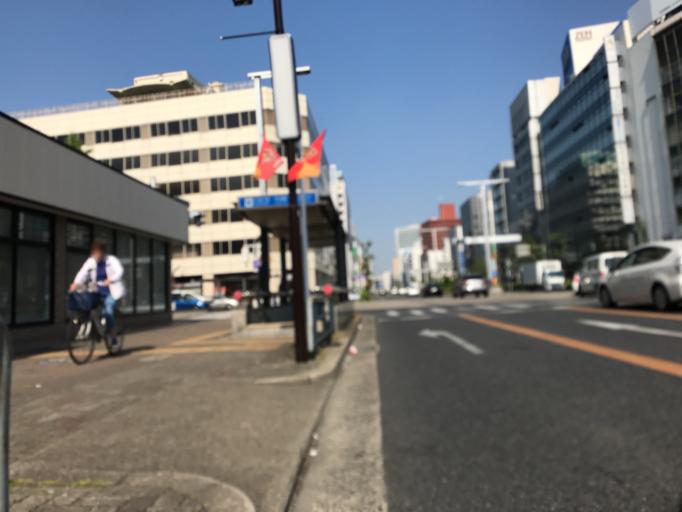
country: JP
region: Aichi
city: Nagoya-shi
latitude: 35.1698
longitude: 136.9377
